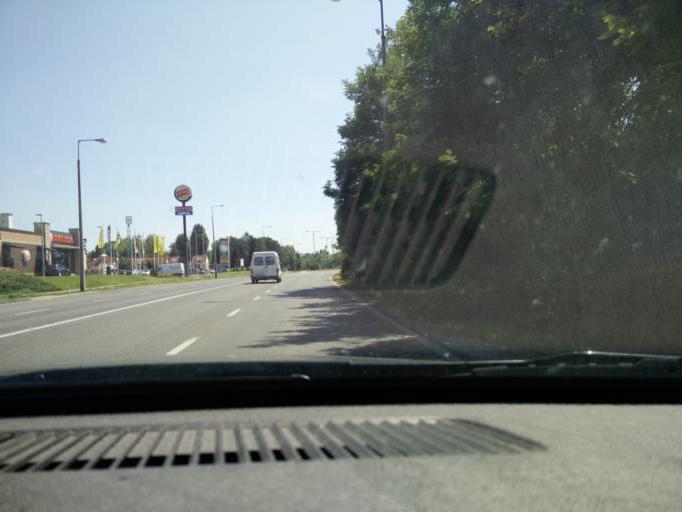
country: HU
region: Komarom-Esztergom
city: Vertesszolos
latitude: 47.6038
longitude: 18.3863
